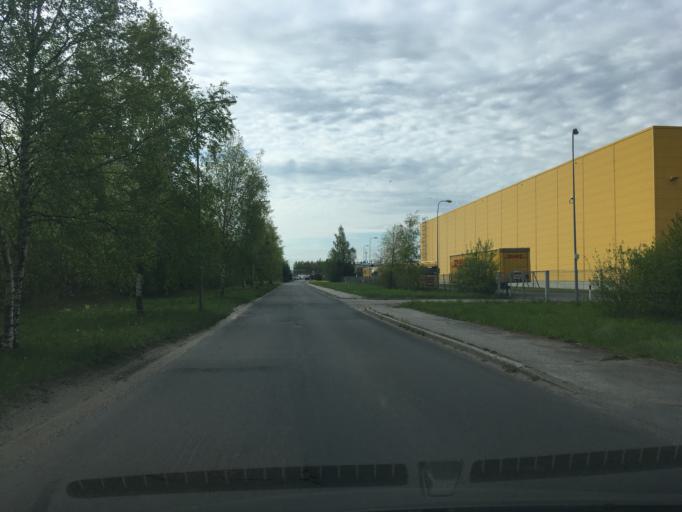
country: EE
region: Harju
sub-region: Tallinna linn
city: Kose
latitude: 59.4301
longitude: 24.8530
